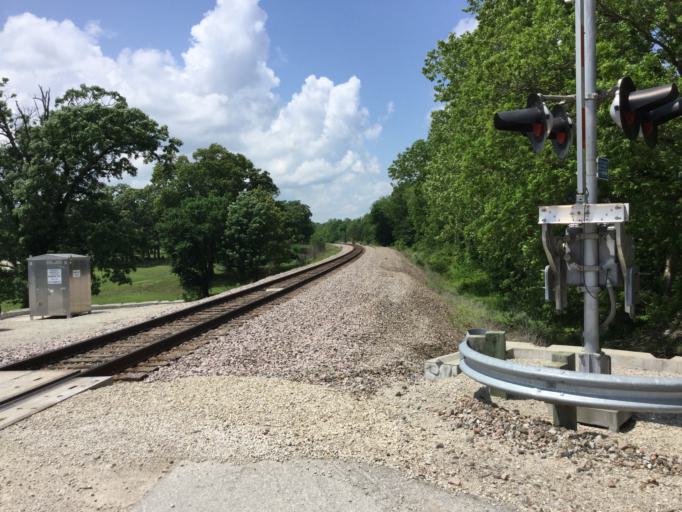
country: US
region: Kansas
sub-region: Linn County
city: La Cygne
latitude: 38.3494
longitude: -94.7656
